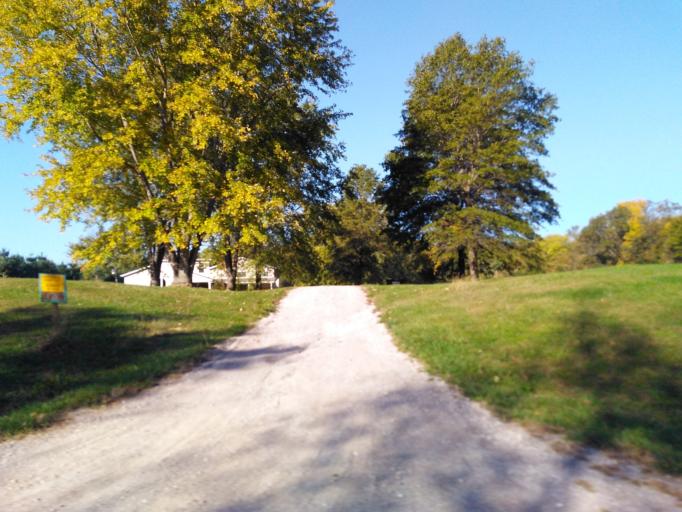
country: US
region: Illinois
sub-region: Madison County
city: Saint Jacob
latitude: 38.7227
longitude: -89.8012
